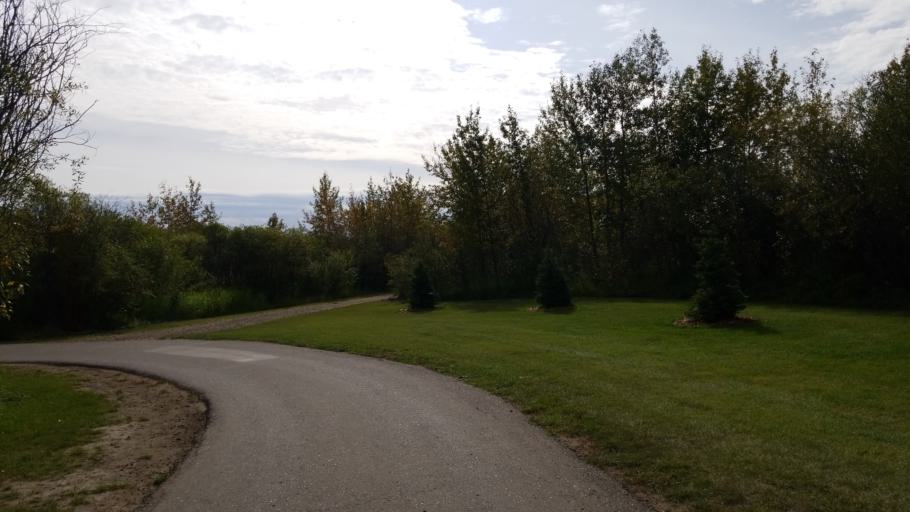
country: CA
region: Saskatchewan
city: Lloydminster
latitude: 53.2617
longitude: -110.0430
